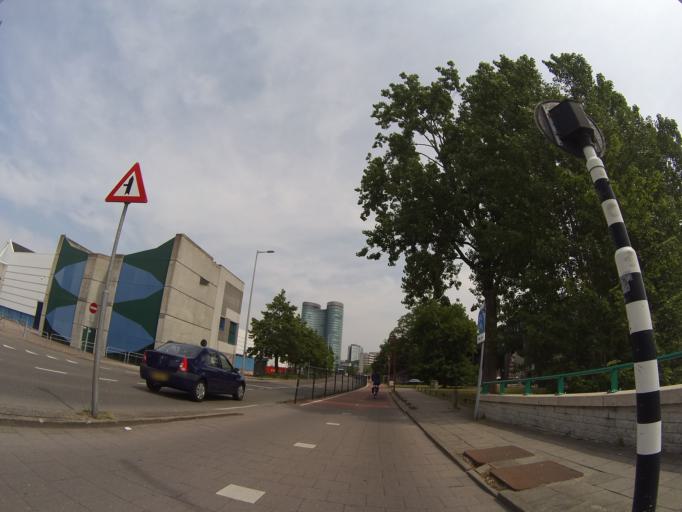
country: NL
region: Utrecht
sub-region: Gemeente Utrecht
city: Utrecht
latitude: 52.0820
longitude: 5.1053
